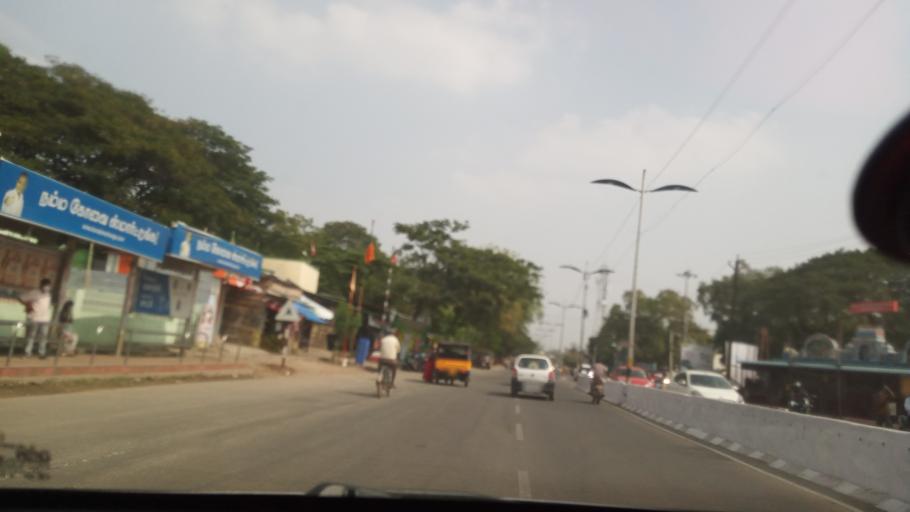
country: IN
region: Tamil Nadu
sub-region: Coimbatore
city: Perur
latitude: 11.0172
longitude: 76.9227
